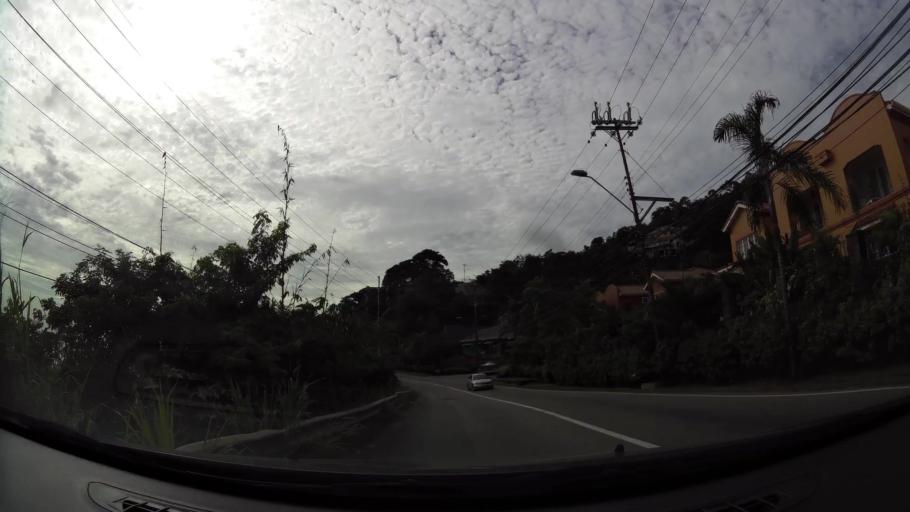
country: TT
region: City of Port of Spain
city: Mucurapo
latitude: 10.6837
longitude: -61.5866
